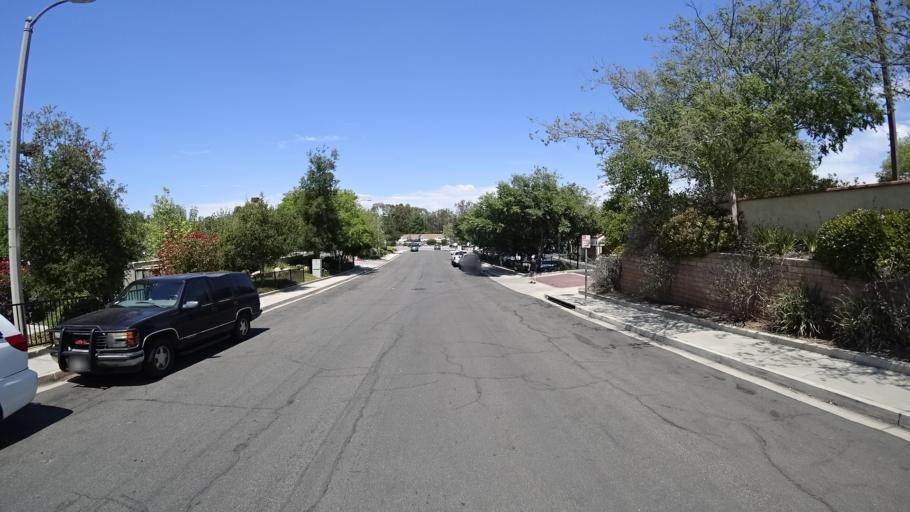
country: US
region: California
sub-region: Ventura County
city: Casa Conejo
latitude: 34.1829
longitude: -118.9164
